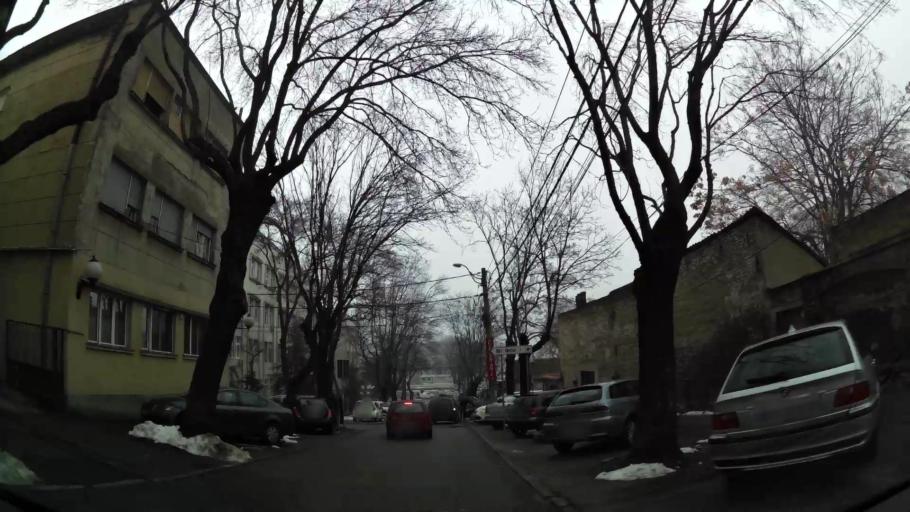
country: RS
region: Central Serbia
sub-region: Belgrade
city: Novi Beograd
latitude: 44.7939
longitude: 20.4373
